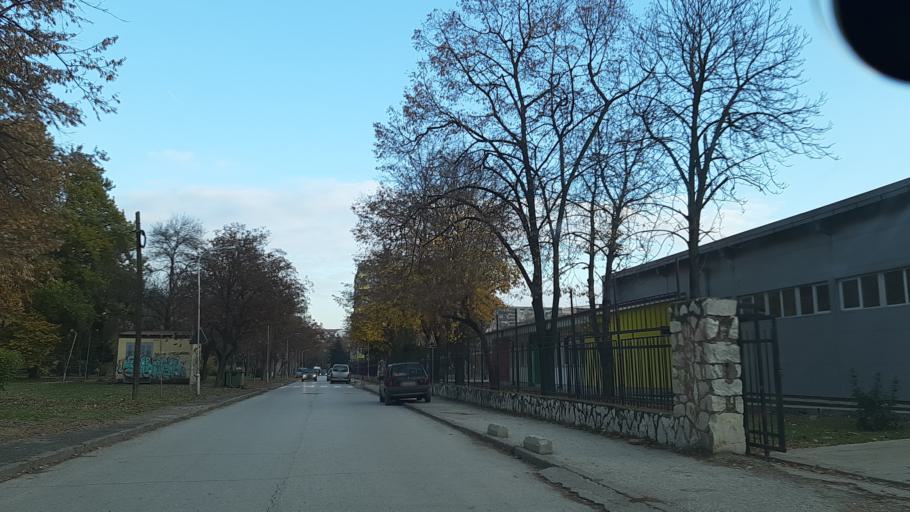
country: MK
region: Karpos
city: Skopje
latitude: 41.9813
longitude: 21.4445
